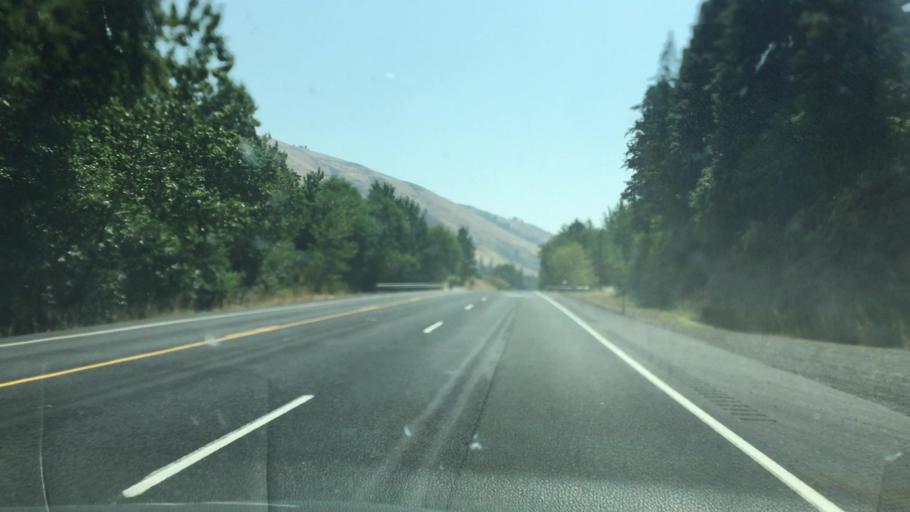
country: US
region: Idaho
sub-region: Nez Perce County
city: Lapwai
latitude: 46.3687
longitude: -116.6473
